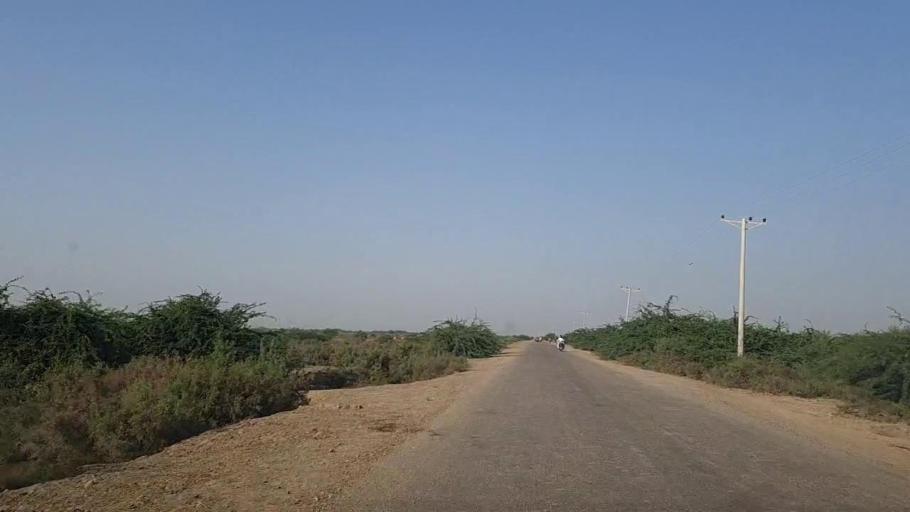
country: PK
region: Sindh
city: Mirpur Batoro
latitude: 24.6047
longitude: 68.4018
